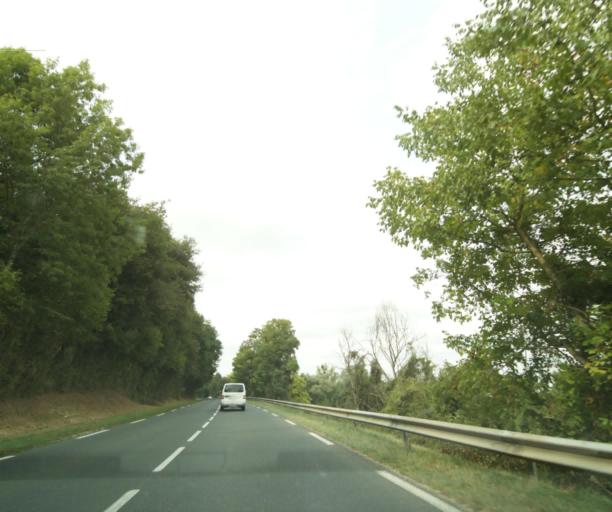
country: FR
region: Centre
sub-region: Departement de l'Indre
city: Clion
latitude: 46.9545
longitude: 1.2160
